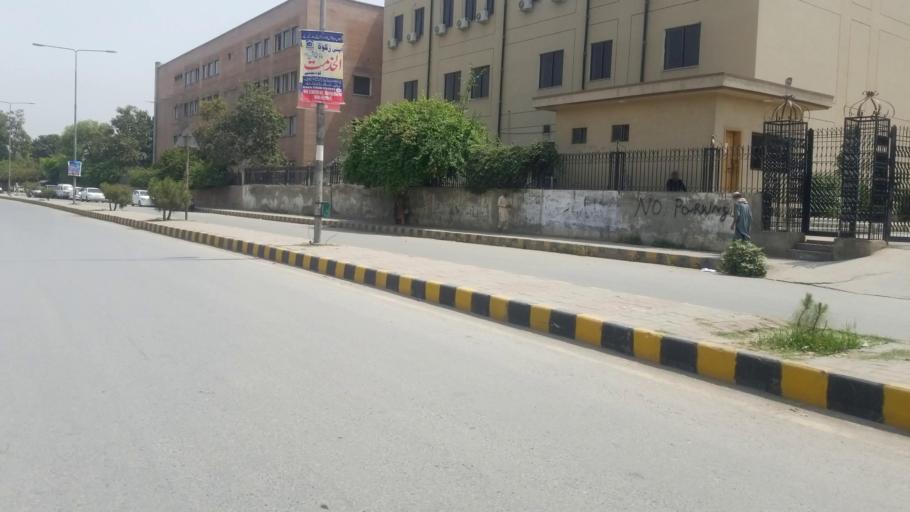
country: PK
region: Khyber Pakhtunkhwa
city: Peshawar
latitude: 33.9938
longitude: 71.4480
